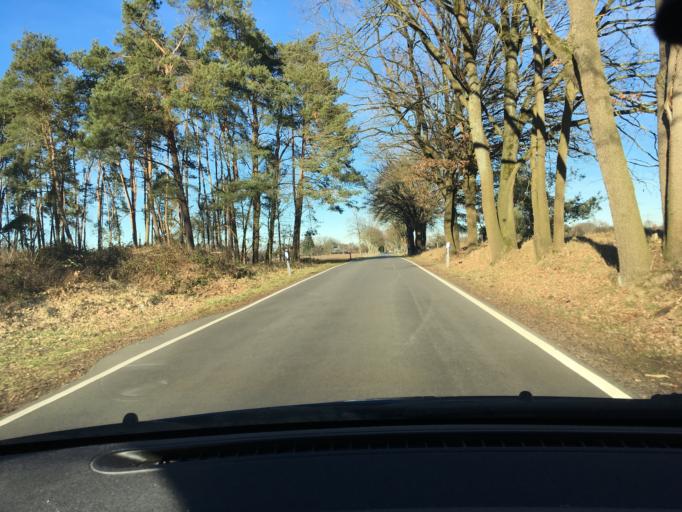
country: DE
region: Lower Saxony
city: Barnstedt
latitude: 53.1515
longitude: 10.3781
